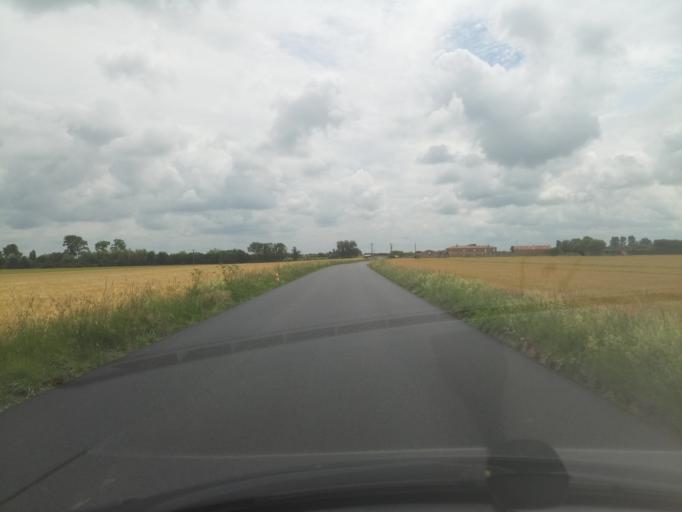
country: FR
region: Poitou-Charentes
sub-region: Departement de la Charente-Maritime
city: Saint-Jean-de-Liversay
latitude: 46.2718
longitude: -0.8984
